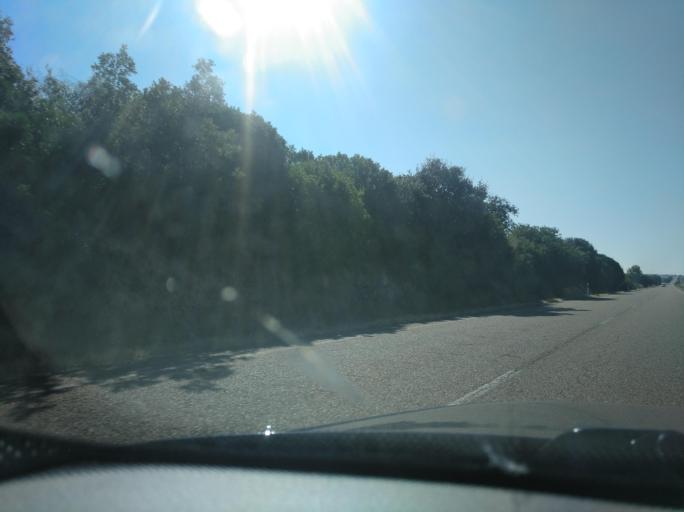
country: ES
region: Extremadura
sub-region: Provincia de Badajoz
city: Olivenza
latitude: 38.7647
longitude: -7.1661
